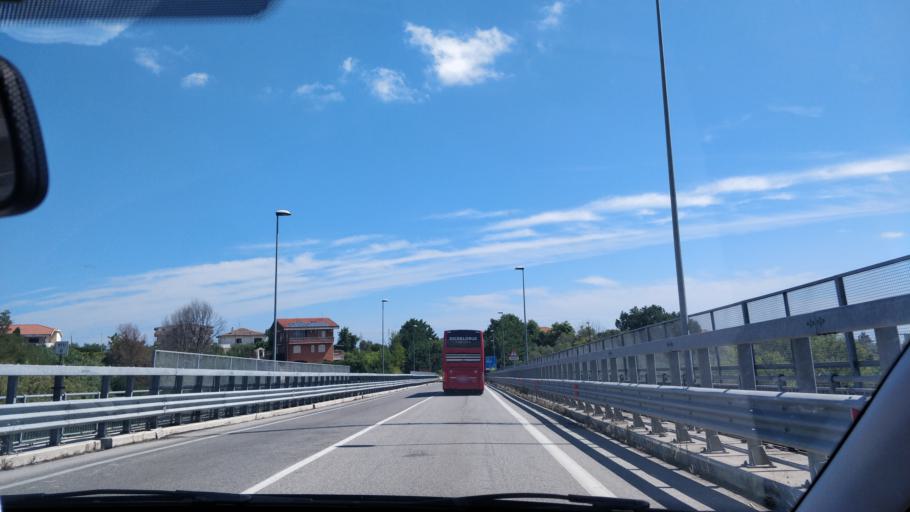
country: IT
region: Abruzzo
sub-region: Provincia di Chieti
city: Francavilla al Mare
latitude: 42.3996
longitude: 14.2963
